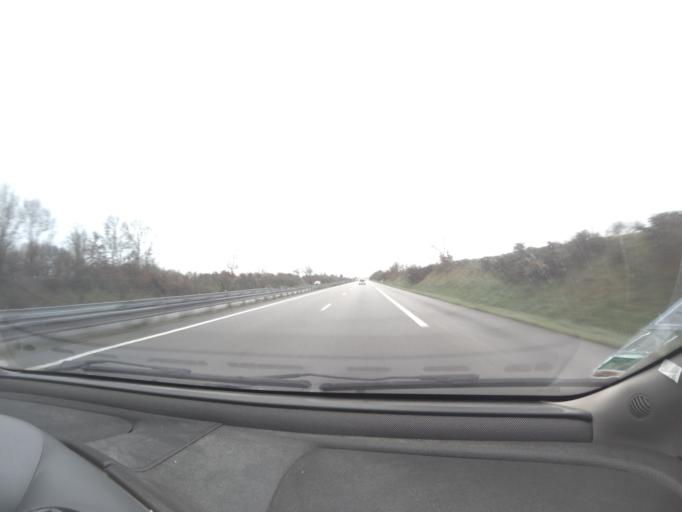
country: FR
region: Pays de la Loire
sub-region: Departement de la Loire-Atlantique
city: Saint-Herblon
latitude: 47.4210
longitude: -1.0616
